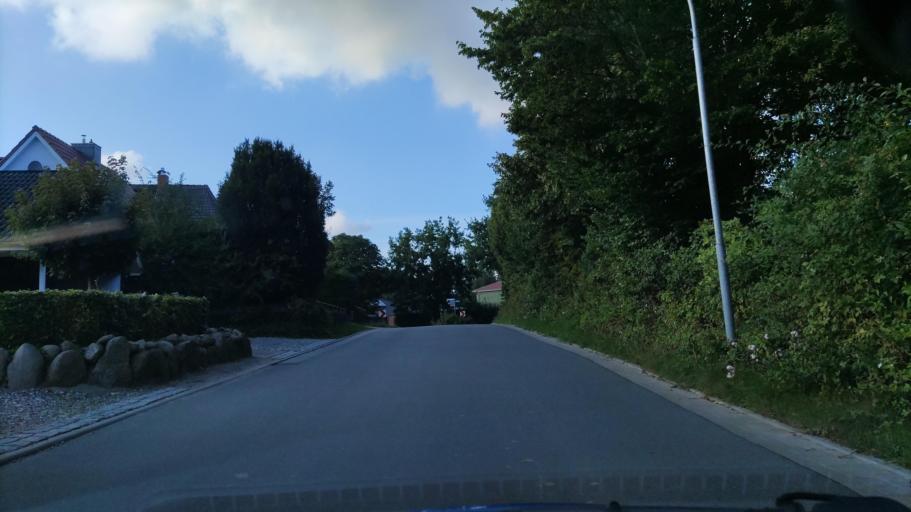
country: DE
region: Schleswig-Holstein
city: Glasau
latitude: 54.0740
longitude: 10.5001
